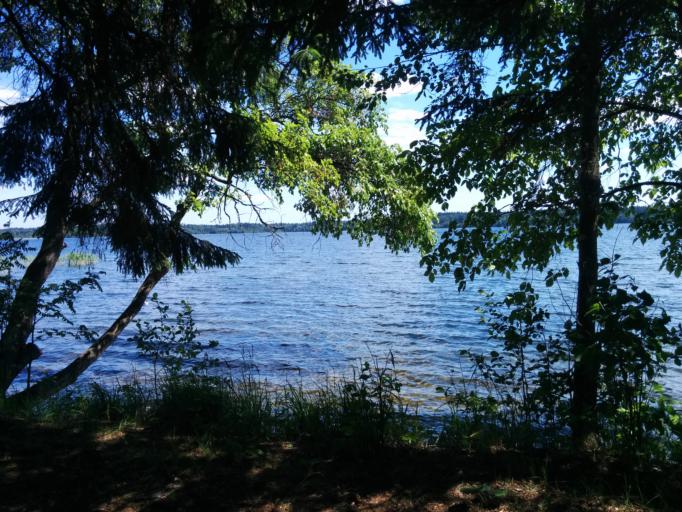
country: RU
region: Novgorod
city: Valday
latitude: 57.9767
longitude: 33.3065
